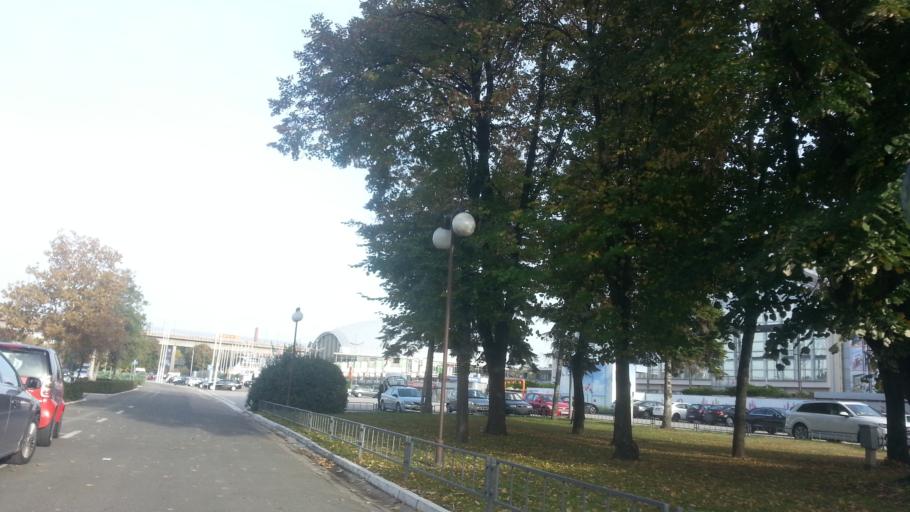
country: RS
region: Central Serbia
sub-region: Belgrade
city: Novi Beograd
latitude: 44.7965
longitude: 20.4355
